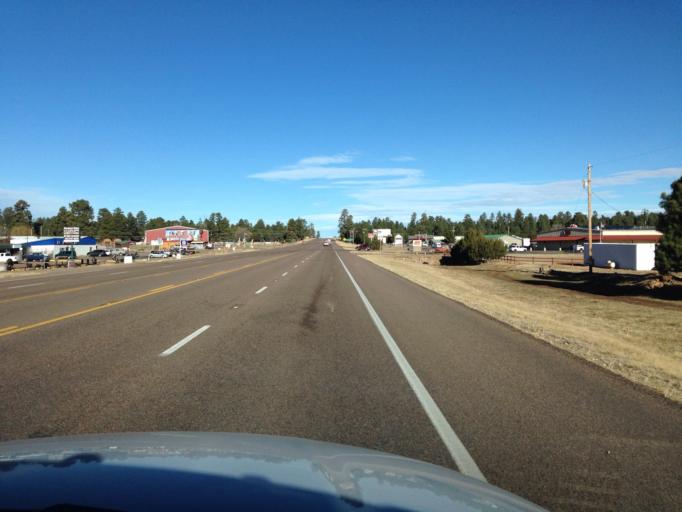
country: US
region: Arizona
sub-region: Navajo County
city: Heber-Overgaard
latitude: 34.4033
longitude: -110.5642
